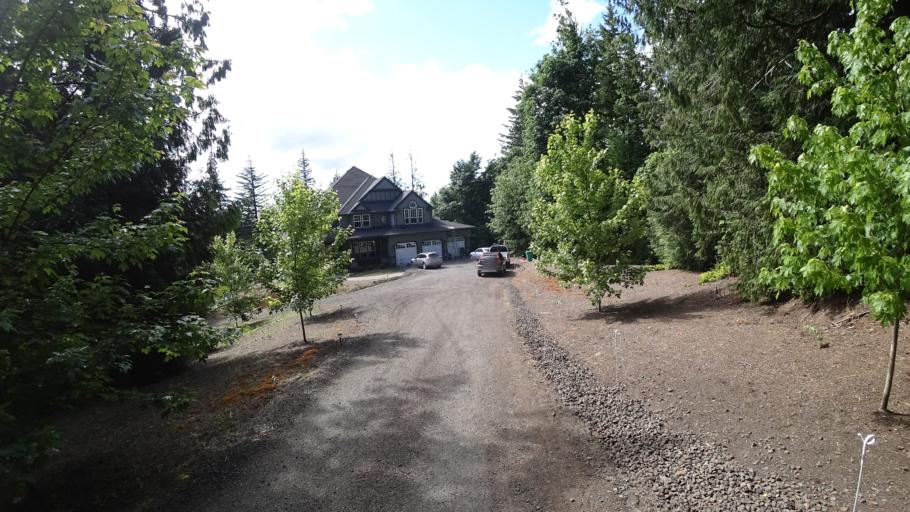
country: US
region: Oregon
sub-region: Washington County
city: Oak Hills
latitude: 45.5781
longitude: -122.8039
